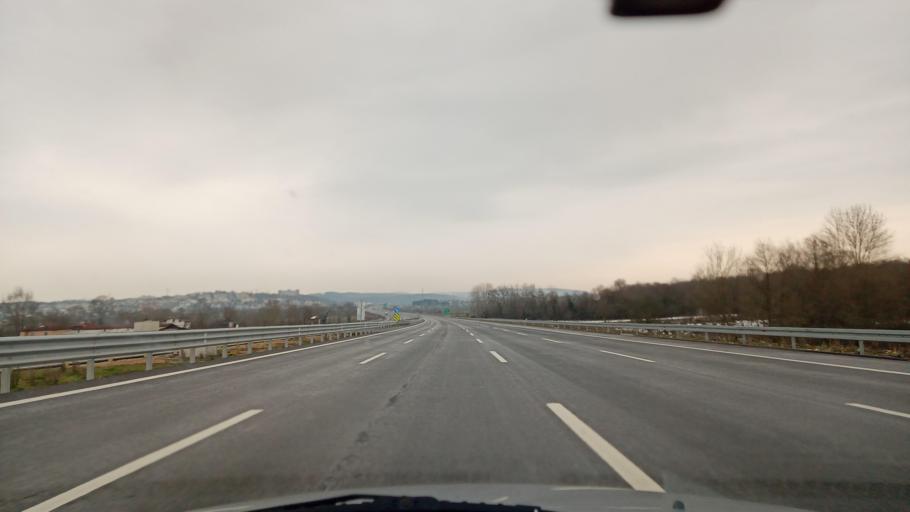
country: TR
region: Sakarya
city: Kazimpasa
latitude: 40.8431
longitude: 30.3047
